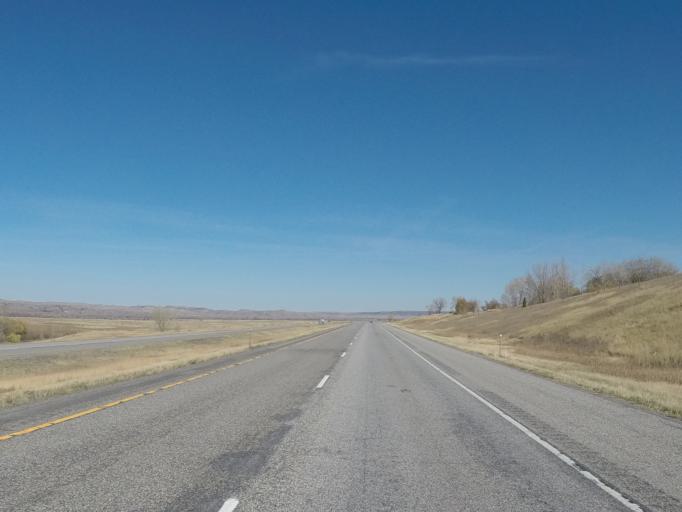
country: US
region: Montana
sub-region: Sweet Grass County
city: Big Timber
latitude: 45.7976
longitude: -110.0324
